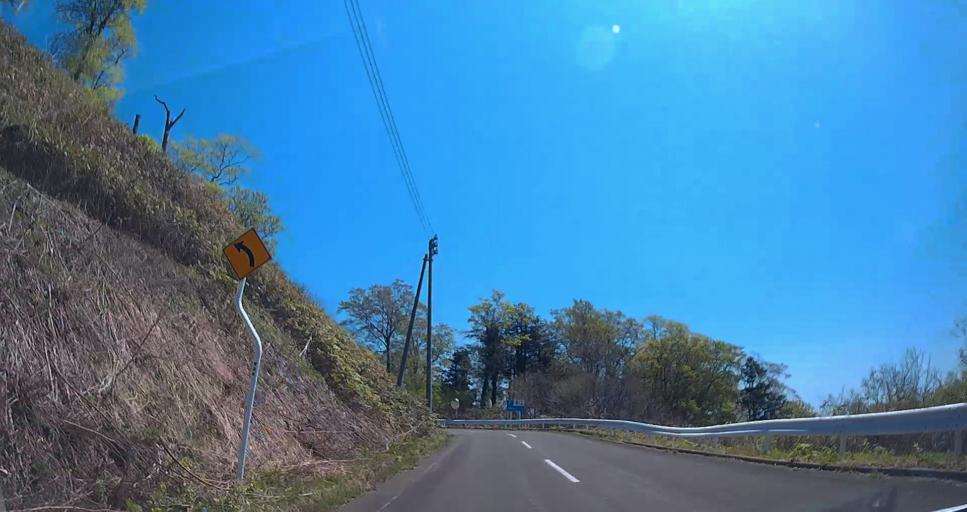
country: JP
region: Aomori
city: Mutsu
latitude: 41.2310
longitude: 140.8156
